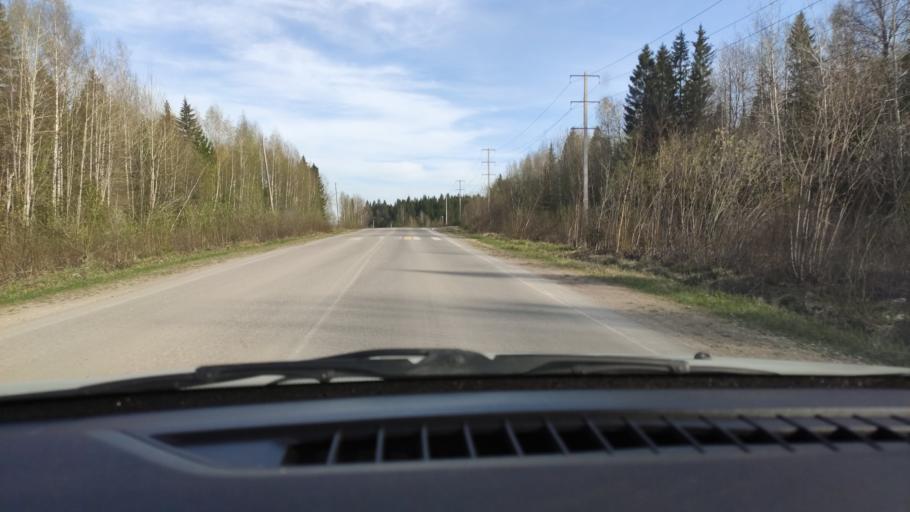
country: RU
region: Perm
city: Novyye Lyady
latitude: 57.9229
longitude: 56.6569
